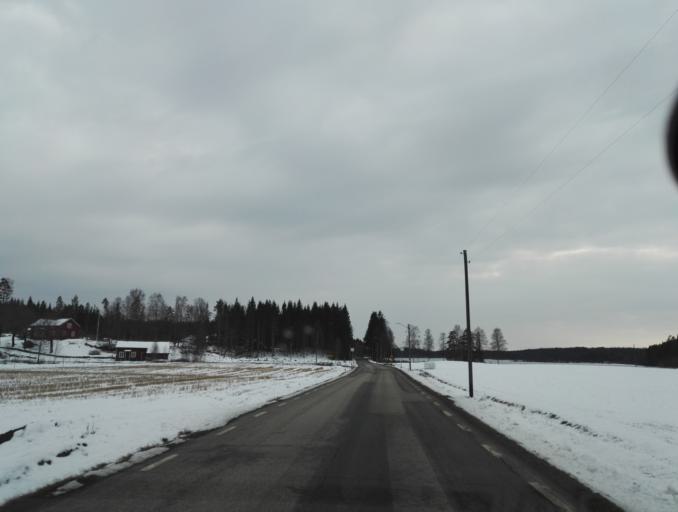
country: SE
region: Vaestra Goetaland
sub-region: Alingsas Kommun
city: Ingared
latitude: 57.7796
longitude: 12.5057
